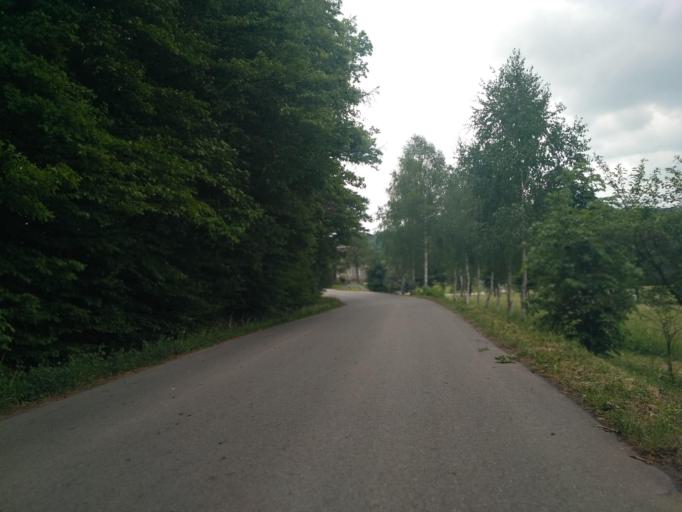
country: PL
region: Subcarpathian Voivodeship
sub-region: Powiat jasielski
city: Nowy Zmigrod
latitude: 49.6567
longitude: 21.5651
